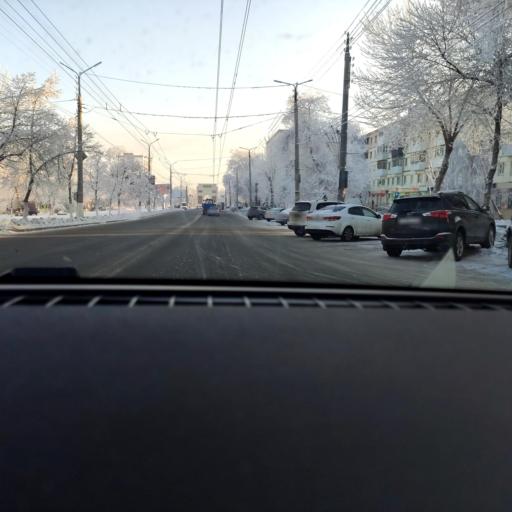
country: RU
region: Samara
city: Novokuybyshevsk
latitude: 53.0977
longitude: 49.9669
